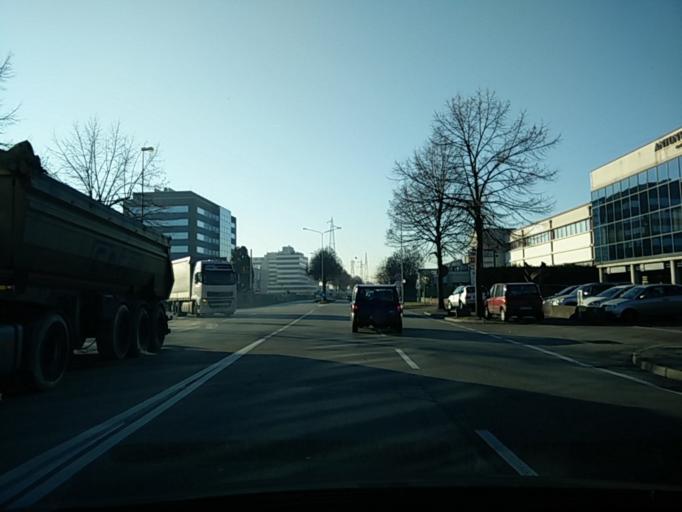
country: IT
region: Veneto
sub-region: Provincia di Padova
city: Noventa
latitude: 45.3957
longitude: 11.9461
